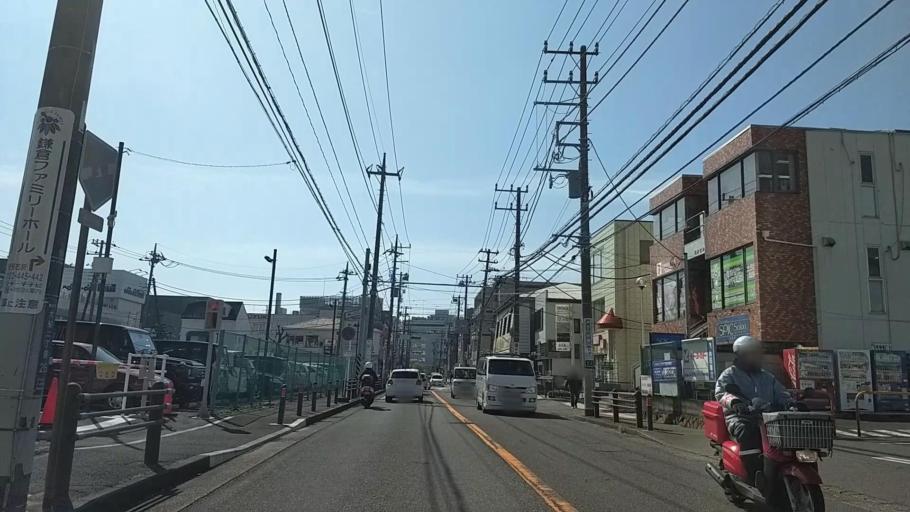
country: JP
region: Kanagawa
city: Kamakura
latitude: 35.3541
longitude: 139.5372
